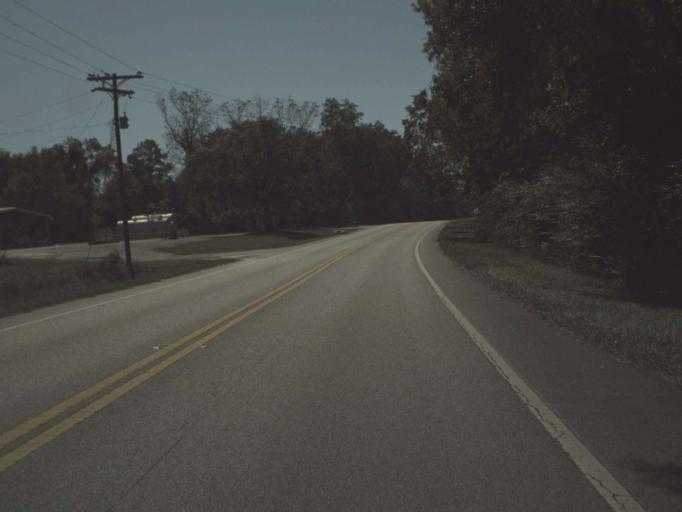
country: US
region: Florida
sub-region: Walton County
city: DeFuniak Springs
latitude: 30.8625
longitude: -86.1156
